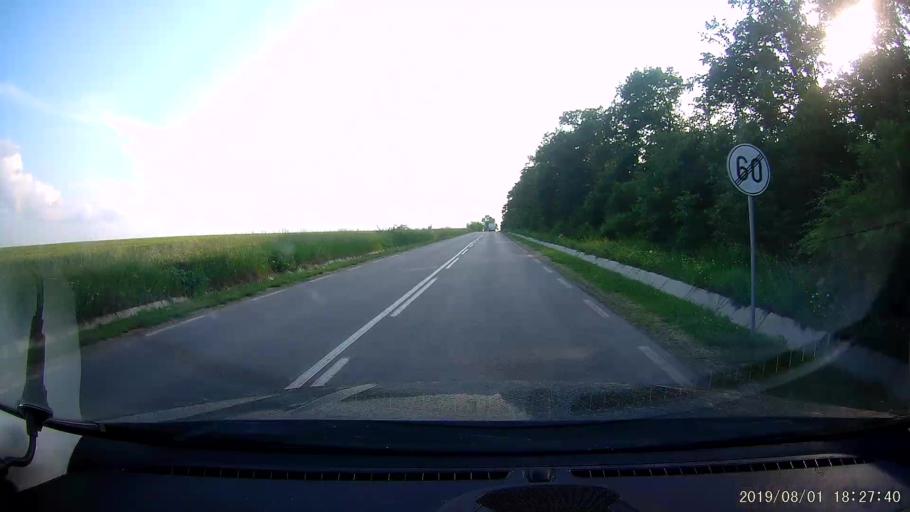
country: BG
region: Shumen
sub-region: Obshtina Venets
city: Venets
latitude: 43.5831
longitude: 26.9795
